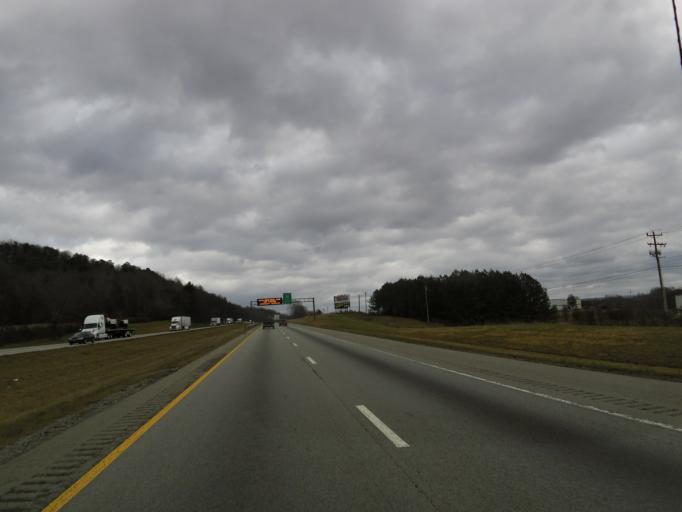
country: US
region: Tennessee
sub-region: Marion County
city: Kimball
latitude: 35.0486
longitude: -85.6531
